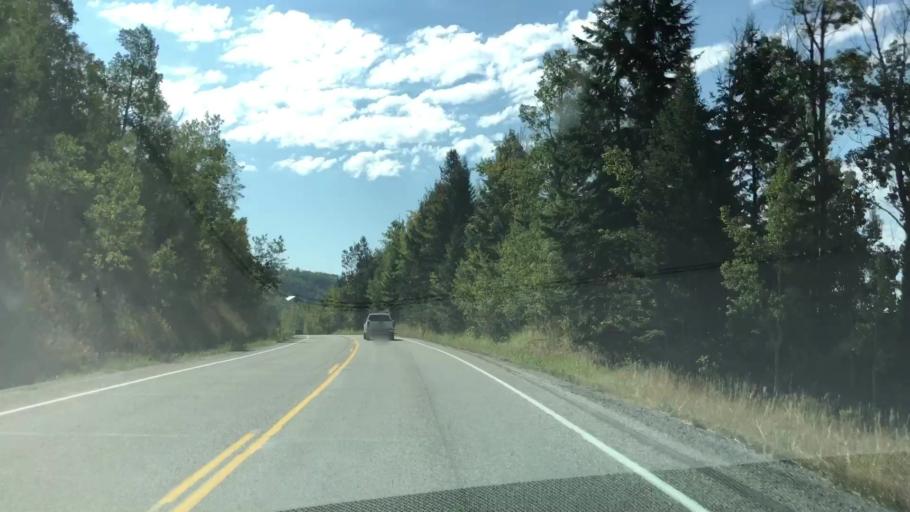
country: US
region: Idaho
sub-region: Teton County
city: Victor
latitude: 43.2814
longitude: -111.1185
